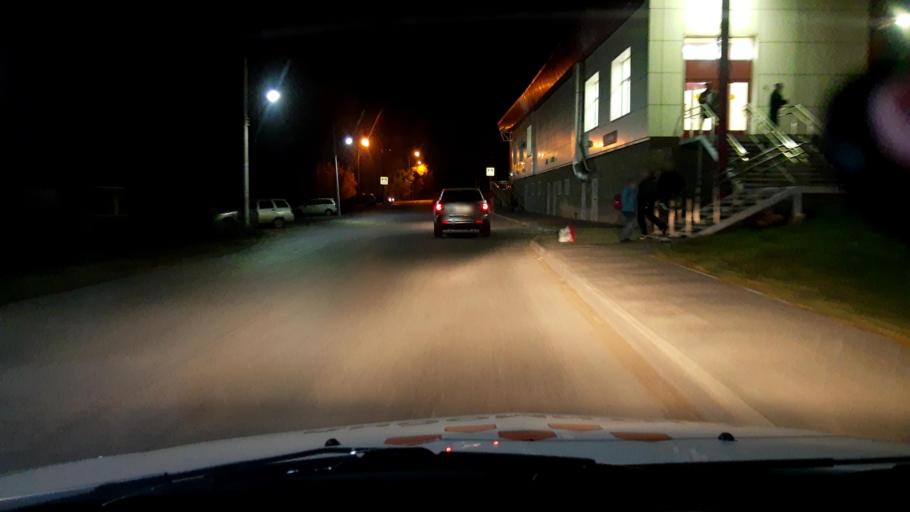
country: RU
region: Bashkortostan
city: Ufa
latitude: 54.7996
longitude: 56.1310
